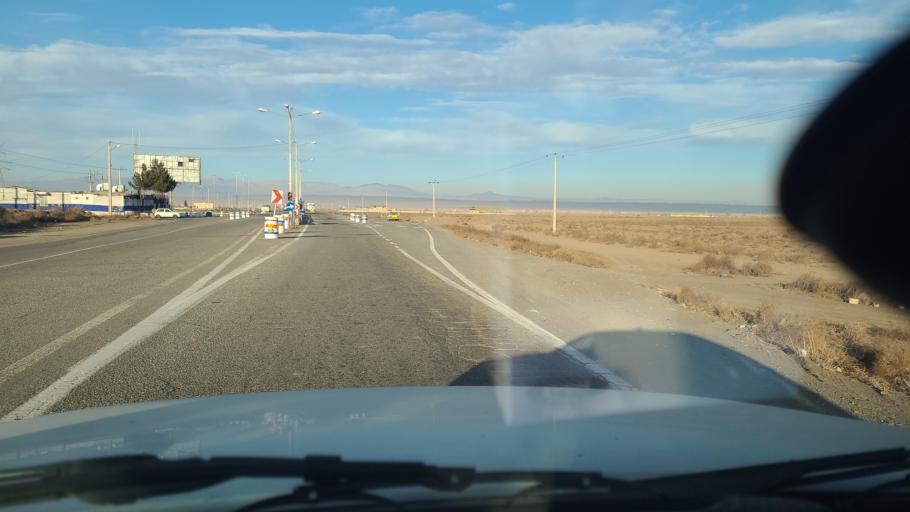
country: IR
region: Razavi Khorasan
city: Neqab
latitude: 36.5837
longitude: 57.5810
